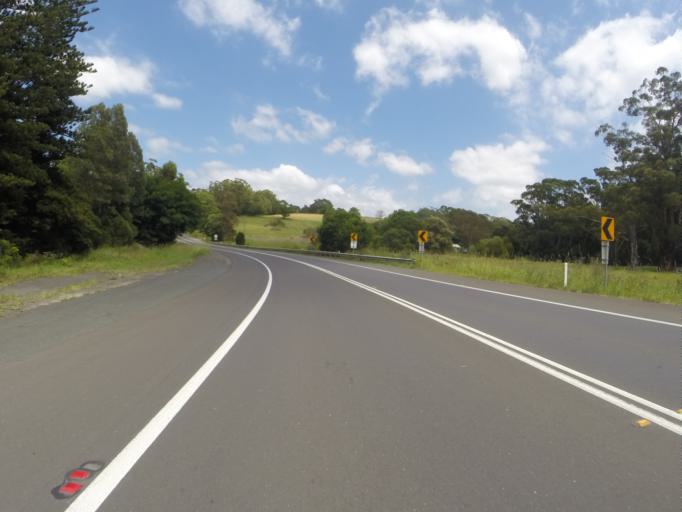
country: AU
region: New South Wales
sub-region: Shoalhaven Shire
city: Berry
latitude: -34.7609
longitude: 150.7372
